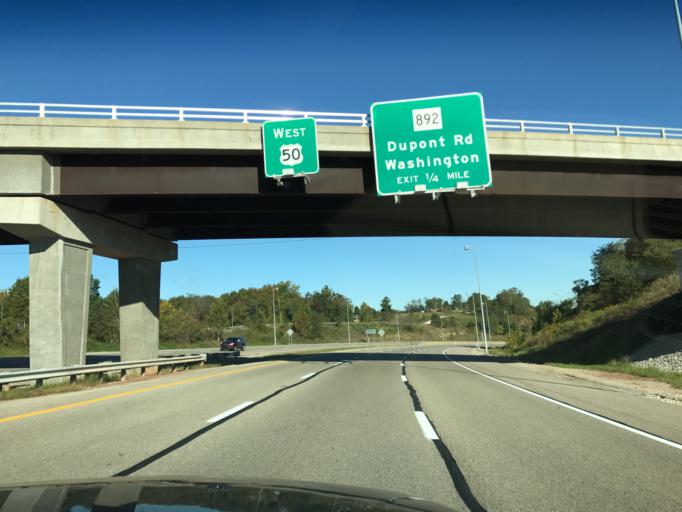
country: US
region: West Virginia
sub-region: Wood County
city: Blennerhassett
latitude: 39.2588
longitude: -81.6445
